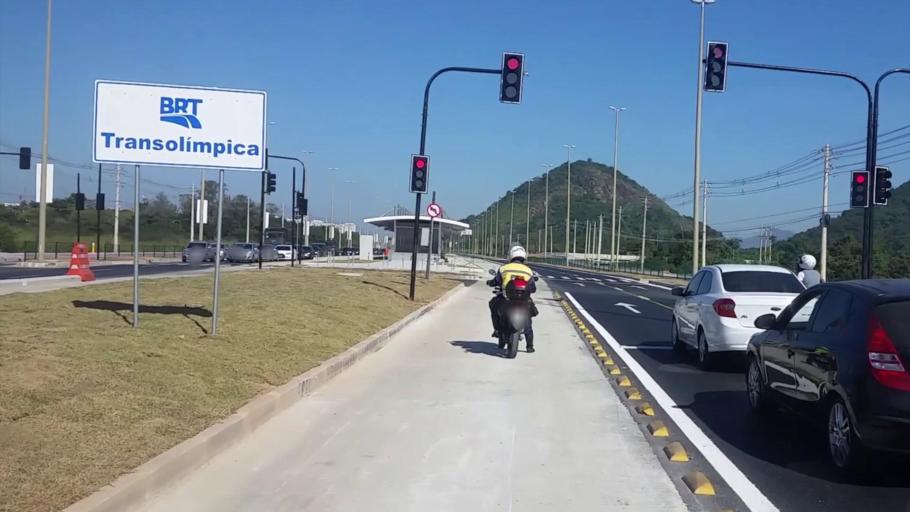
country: BR
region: Rio de Janeiro
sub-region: Nilopolis
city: Nilopolis
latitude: -22.9832
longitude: -43.4114
